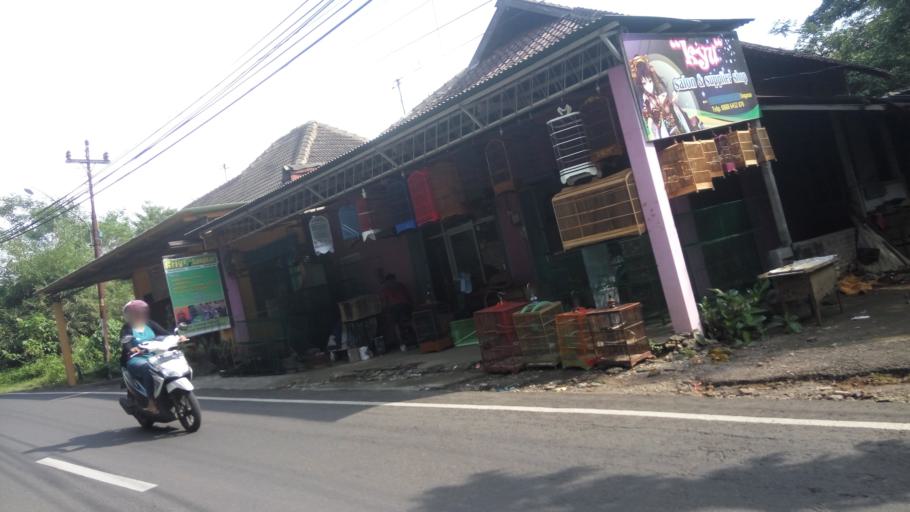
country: ID
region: Central Java
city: Ungaran
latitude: -7.1431
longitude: 110.4154
